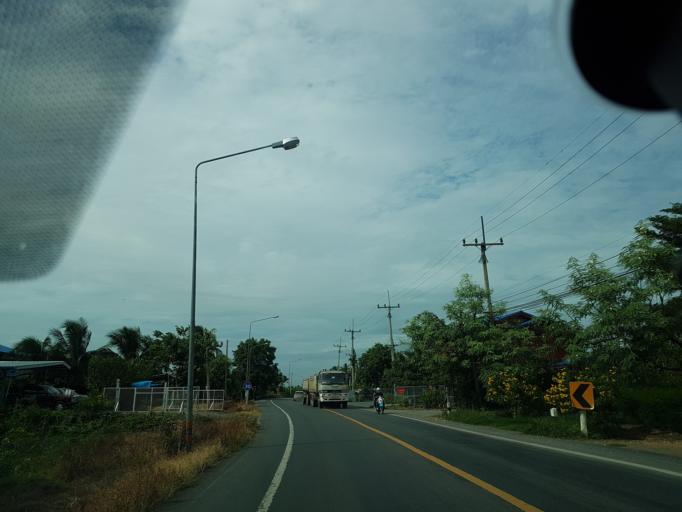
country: TH
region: Lop Buri
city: Tha Wung
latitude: 14.7655
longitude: 100.5654
